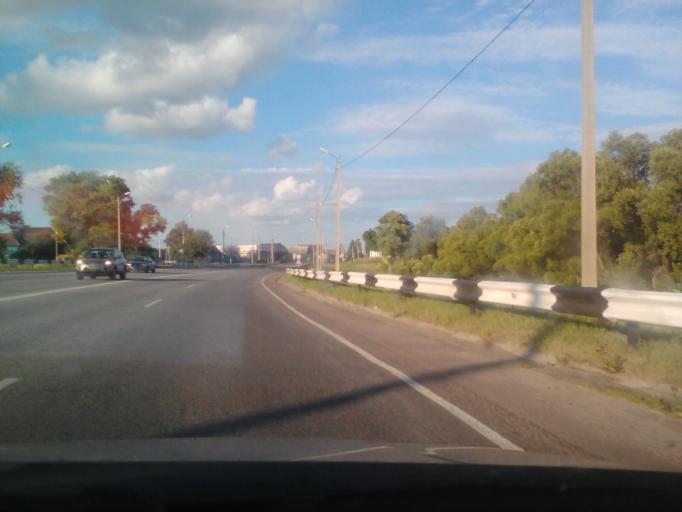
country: RU
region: Kursk
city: Kurchatov
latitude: 51.6664
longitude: 35.7323
